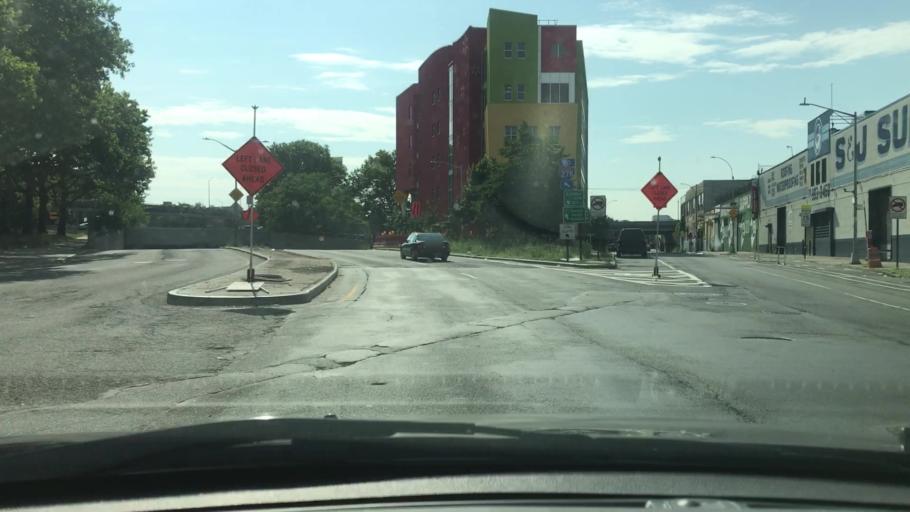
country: US
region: New York
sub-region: New York County
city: Manhattan
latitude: 40.8033
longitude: -73.9189
